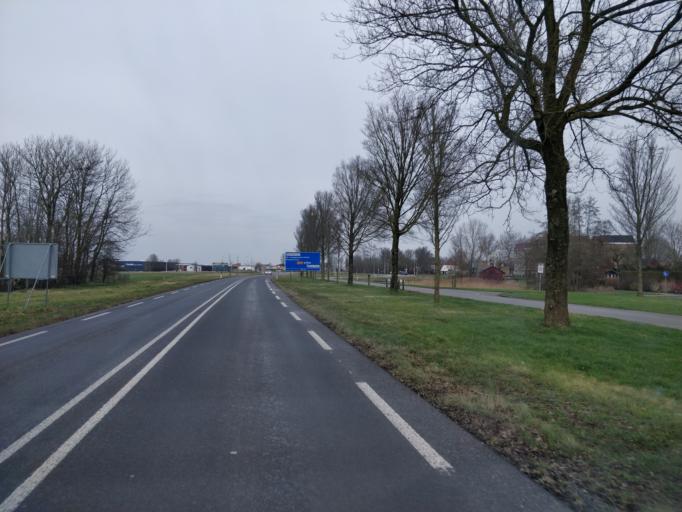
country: NL
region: Friesland
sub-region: Gemeente Leeuwarderadeel
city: Stiens
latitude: 53.2623
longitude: 5.7530
